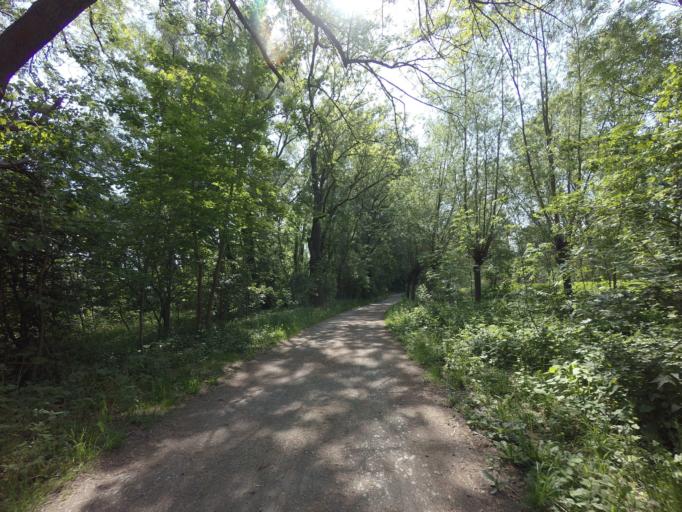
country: DE
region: Lower Saxony
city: Braunschweig
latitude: 52.2730
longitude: 10.5629
